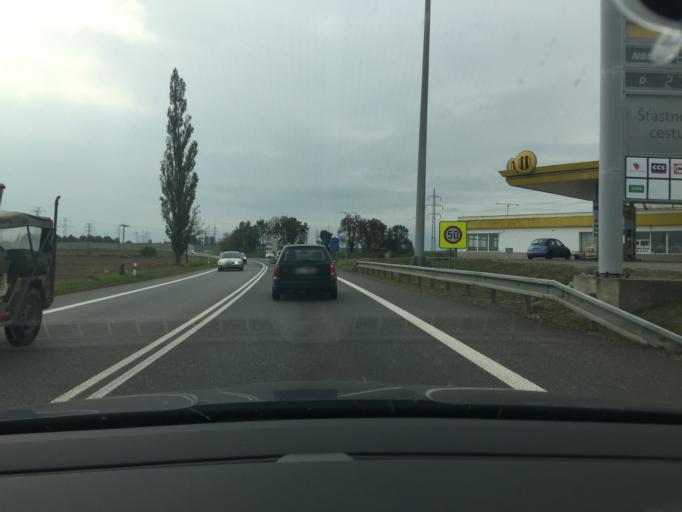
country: CZ
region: Jihocesky
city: Mirovice
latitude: 49.5238
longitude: 14.0727
